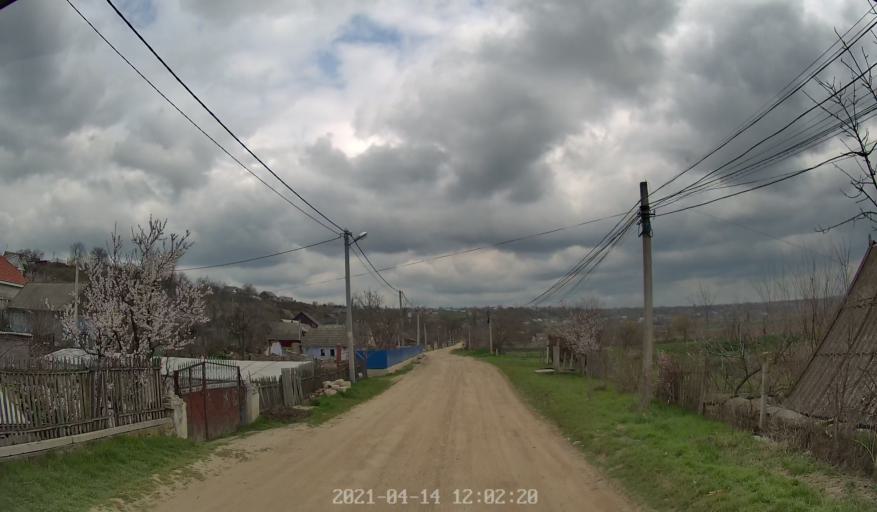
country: MD
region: Criuleni
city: Criuleni
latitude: 47.1668
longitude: 29.2041
